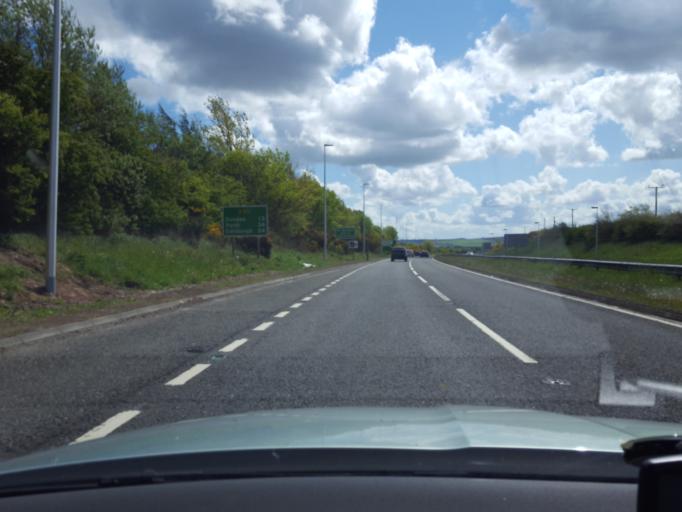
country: GB
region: Scotland
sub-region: Angus
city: Forfar
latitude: 56.6179
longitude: -2.9030
